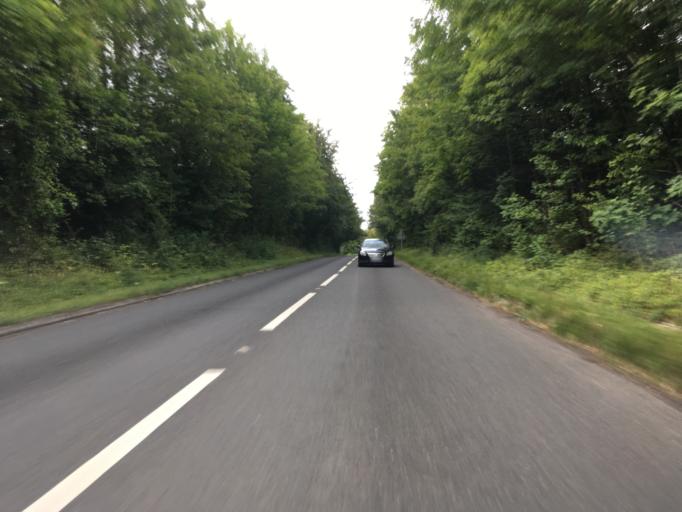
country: GB
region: England
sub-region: Hampshire
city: Overton
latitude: 51.1912
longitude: -1.2557
